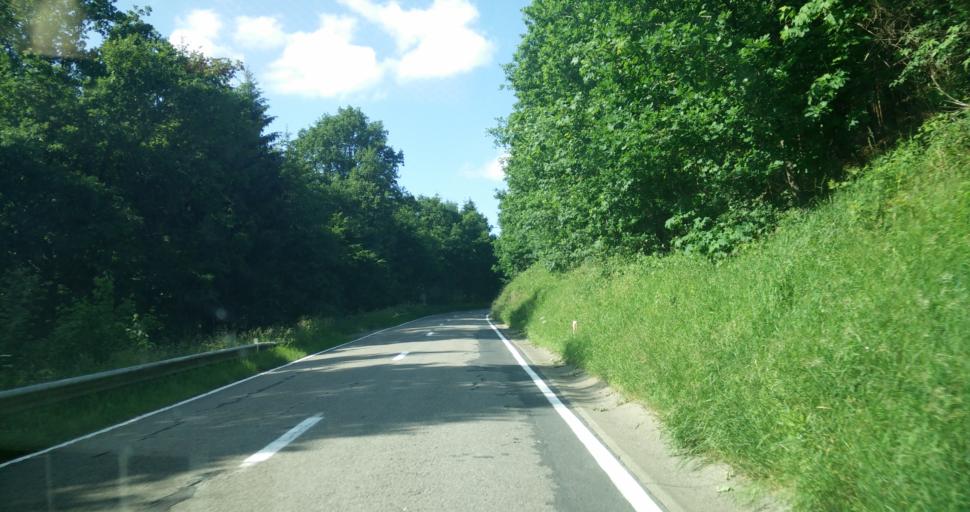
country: BE
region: Wallonia
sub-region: Province du Luxembourg
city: Houffalize
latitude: 50.1409
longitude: 5.7175
